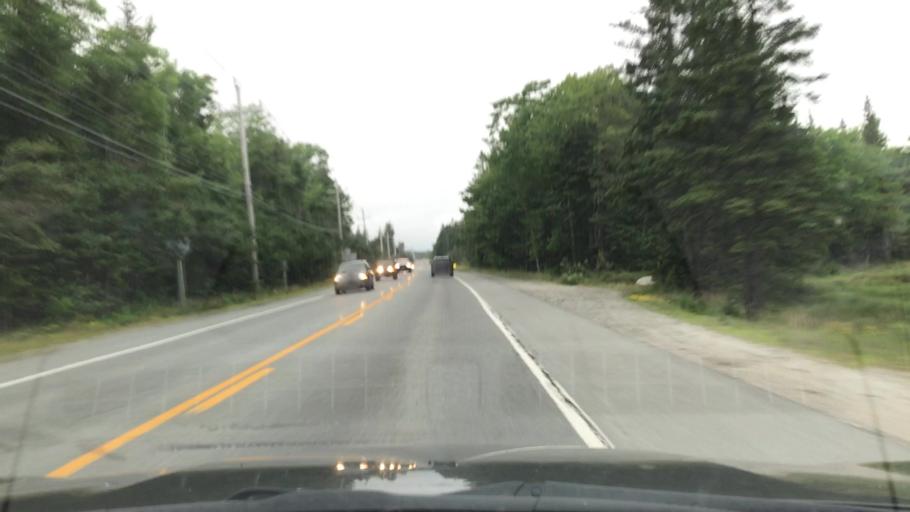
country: US
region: Maine
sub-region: Hancock County
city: Trenton
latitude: 44.4231
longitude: -68.3645
